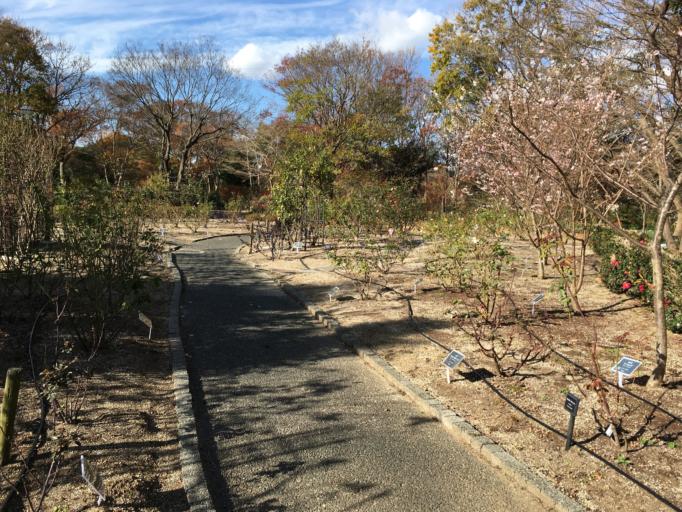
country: JP
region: Aichi
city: Toyohashi
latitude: 34.7216
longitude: 137.4346
